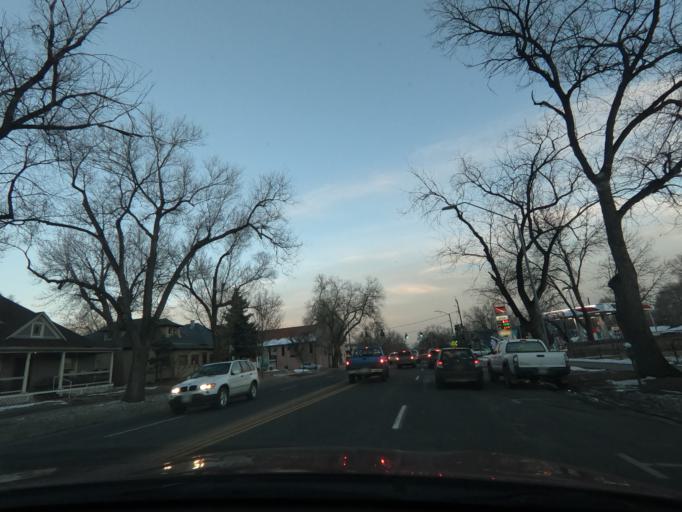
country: US
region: Colorado
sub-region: El Paso County
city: Colorado Springs
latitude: 38.8440
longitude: -104.8574
